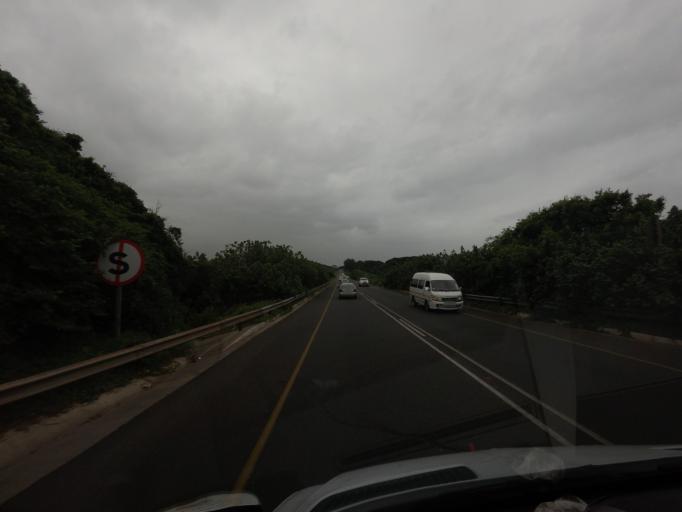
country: ZA
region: KwaZulu-Natal
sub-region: eThekwini Metropolitan Municipality
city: Durban
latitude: -29.7043
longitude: 31.0976
